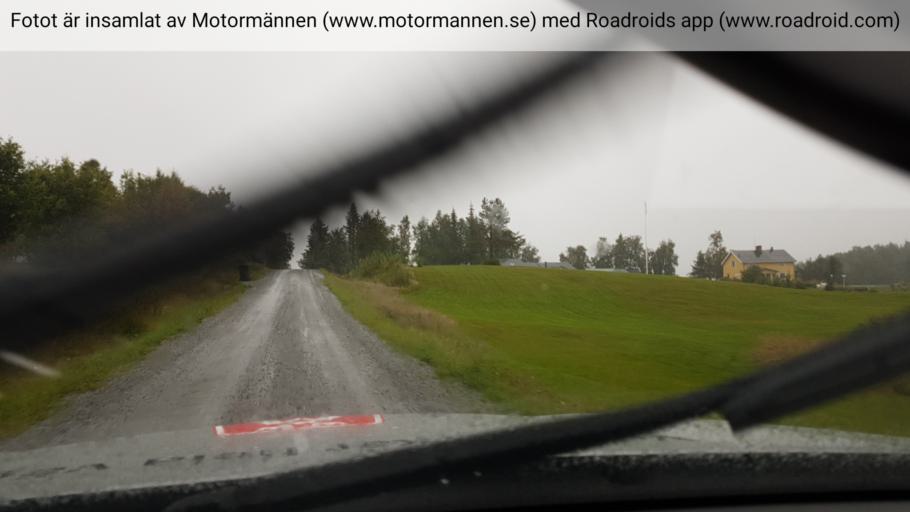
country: SE
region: Norrbotten
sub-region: Jokkmokks Kommun
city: Jokkmokk
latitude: 66.6909
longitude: 18.8042
